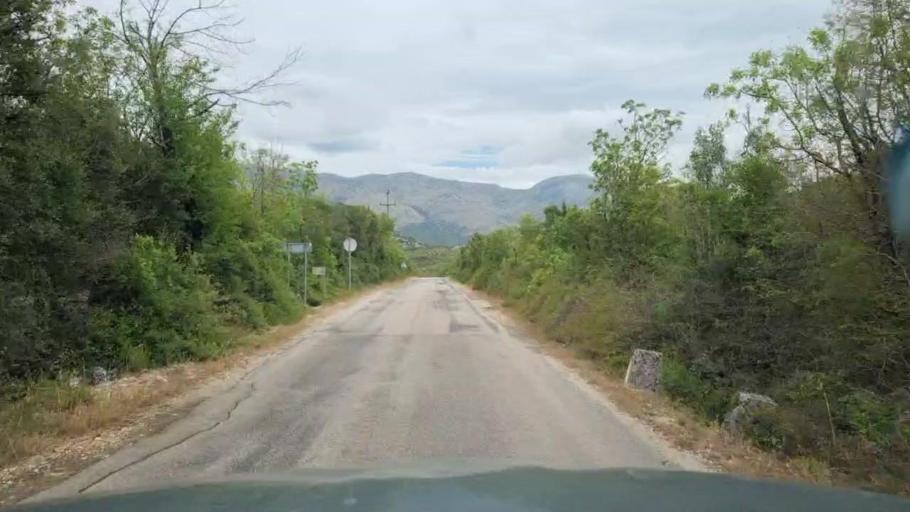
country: BA
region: Federation of Bosnia and Herzegovina
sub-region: Hercegovacko-Bosanski Kanton
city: Neum
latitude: 42.9426
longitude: 17.6931
